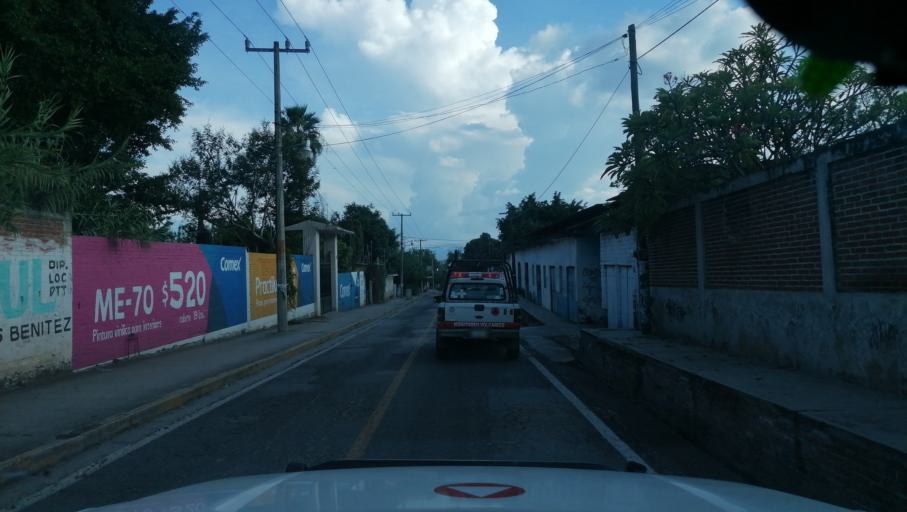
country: MX
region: Morelos
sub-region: Ayala
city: Abelardo L. Rodriguez
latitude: 18.7201
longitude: -98.9916
